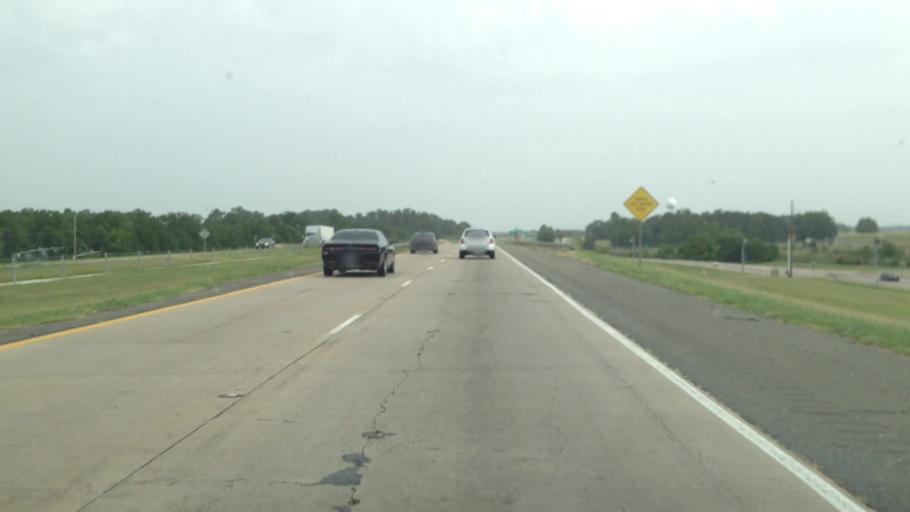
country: US
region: Louisiana
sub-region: Caddo Parish
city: Shreveport
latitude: 32.4405
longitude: -93.8416
